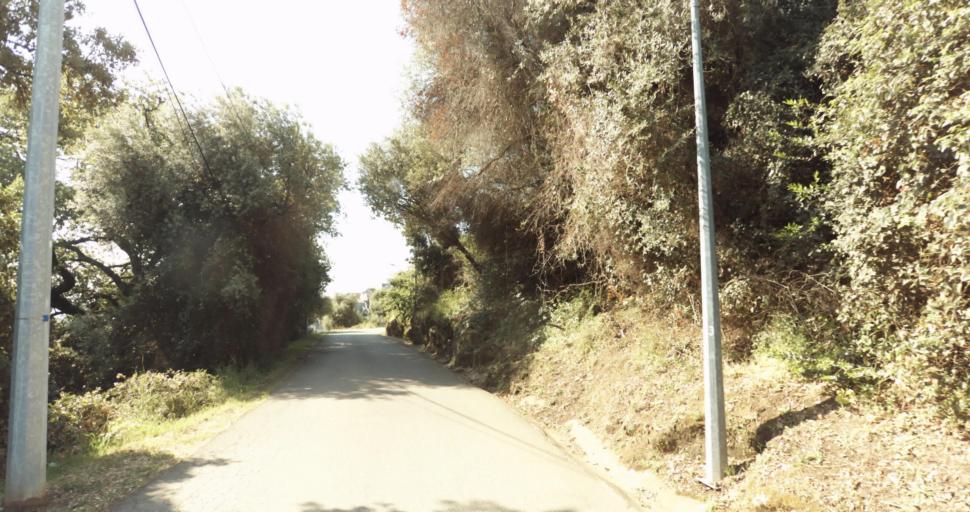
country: FR
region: Corsica
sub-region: Departement de la Haute-Corse
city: Biguglia
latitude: 42.6293
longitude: 9.4186
